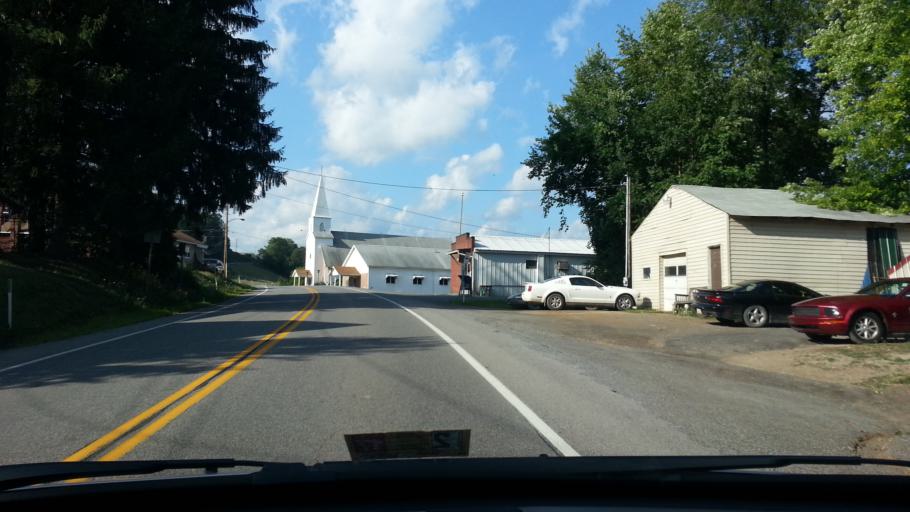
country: US
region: Pennsylvania
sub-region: Elk County
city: Saint Marys
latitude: 41.2568
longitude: -78.5019
